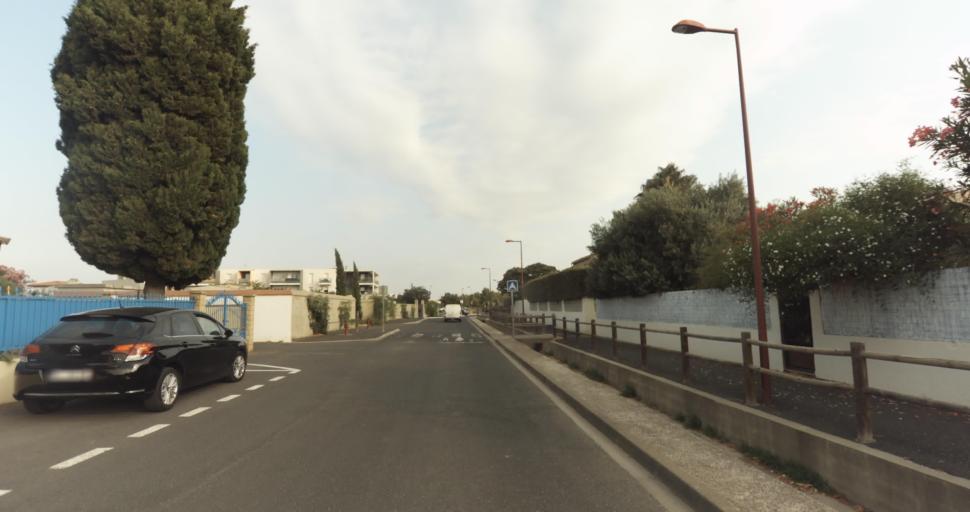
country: FR
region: Languedoc-Roussillon
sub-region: Departement des Pyrenees-Orientales
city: Theza
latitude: 42.6401
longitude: 2.9511
